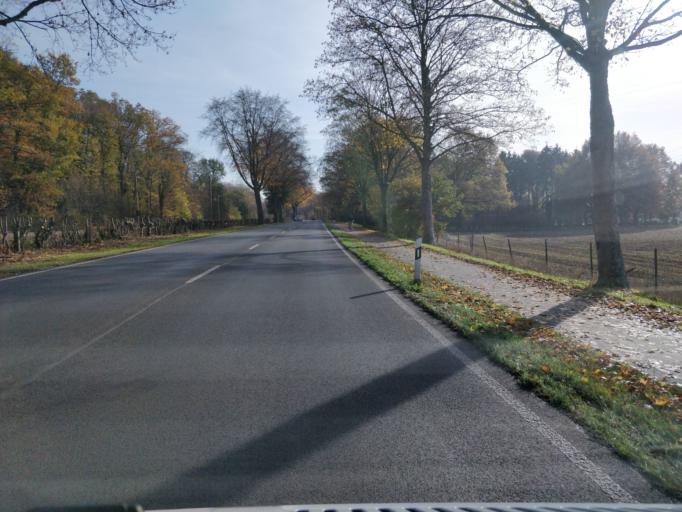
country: DE
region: North Rhine-Westphalia
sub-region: Regierungsbezirk Dusseldorf
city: Mehrhoog
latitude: 51.7628
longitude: 6.4702
